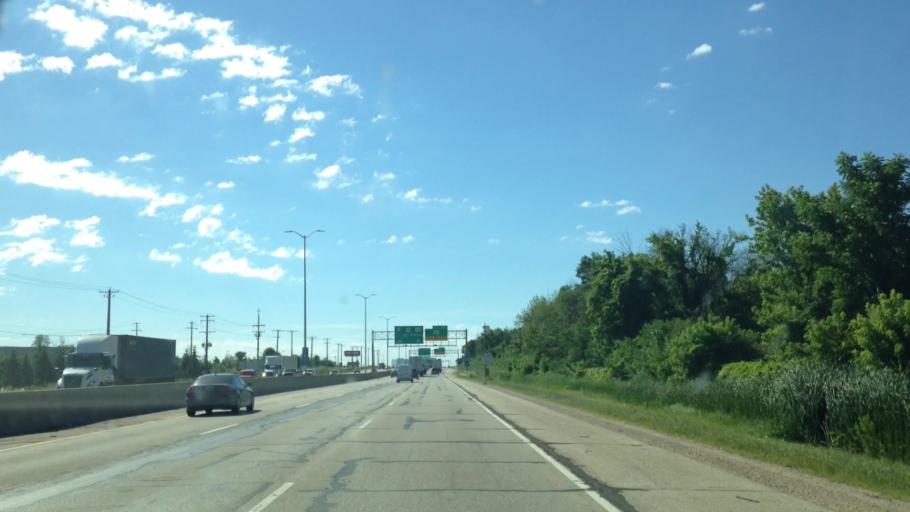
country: US
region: Wisconsin
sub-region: Waukesha County
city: Menomonee Falls
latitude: 43.1675
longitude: -88.0747
